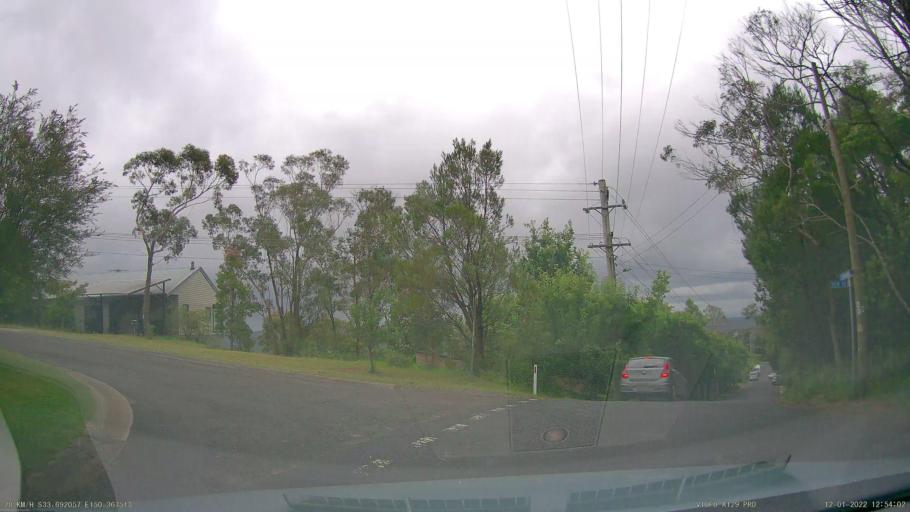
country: AU
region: New South Wales
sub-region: Blue Mountains Municipality
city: Leura
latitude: -33.6919
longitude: 150.3676
